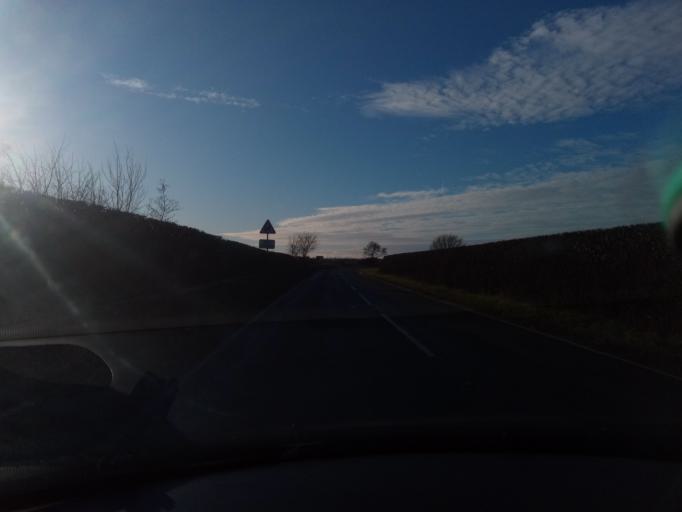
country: GB
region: England
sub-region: North Yorkshire
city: Ripon
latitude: 54.2213
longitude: -1.4769
